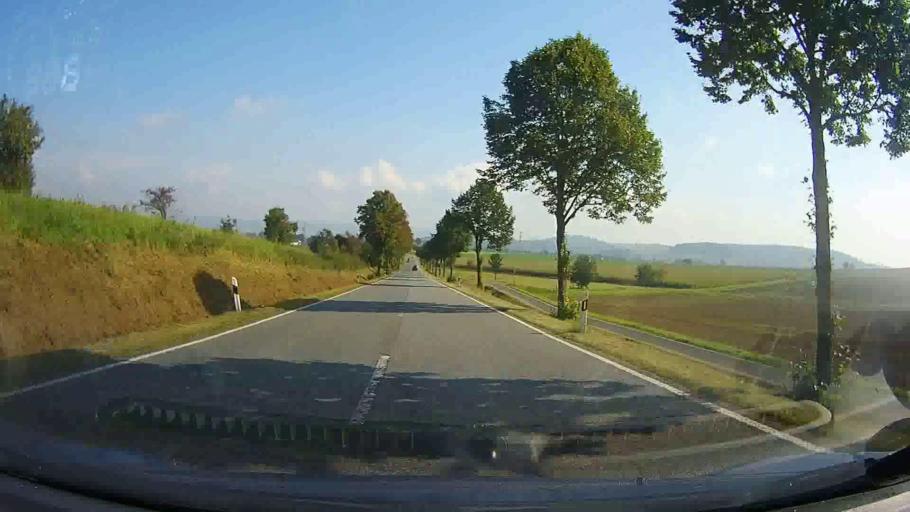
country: DE
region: Lower Saxony
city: Moringen
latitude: 51.6997
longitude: 9.8978
